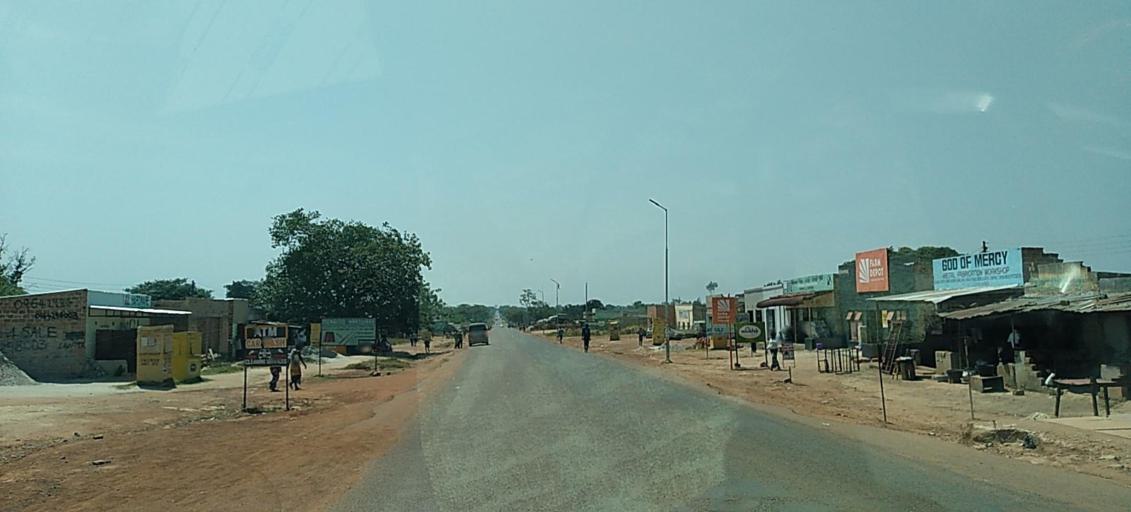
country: ZM
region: North-Western
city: Solwezi
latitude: -12.3139
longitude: 25.8519
